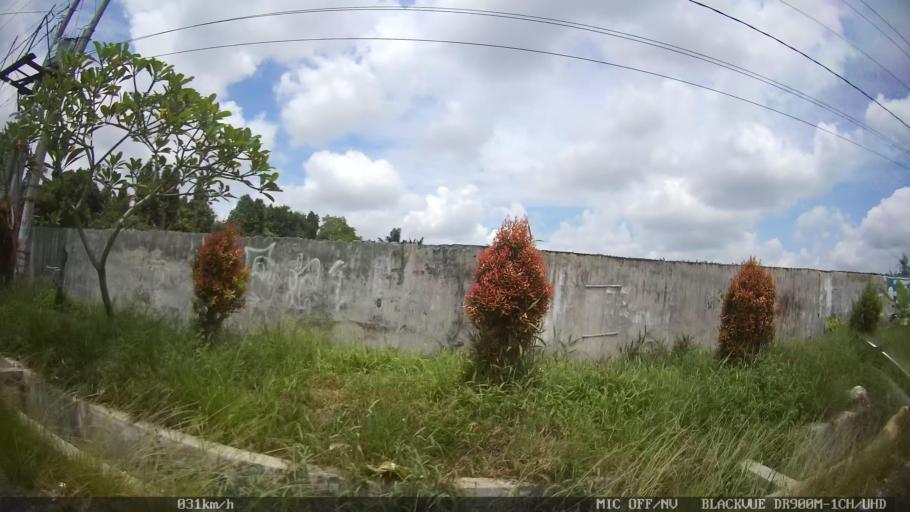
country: ID
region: North Sumatra
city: Medan
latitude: 3.6119
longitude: 98.7480
